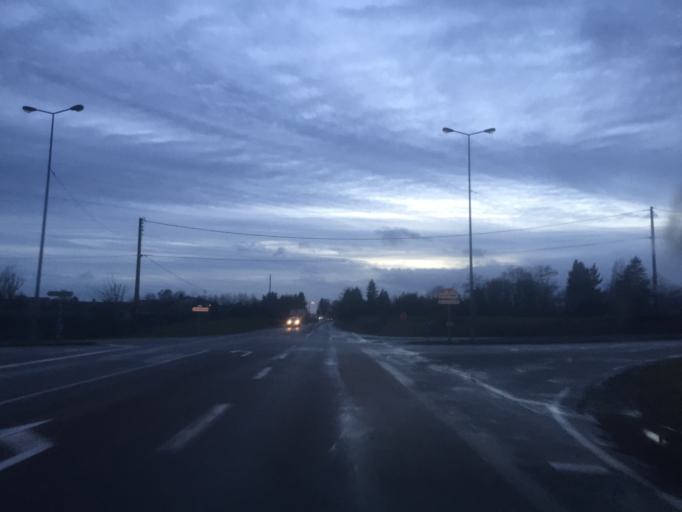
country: FR
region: Franche-Comte
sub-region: Departement du Jura
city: Dole
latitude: 47.1061
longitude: 5.5188
